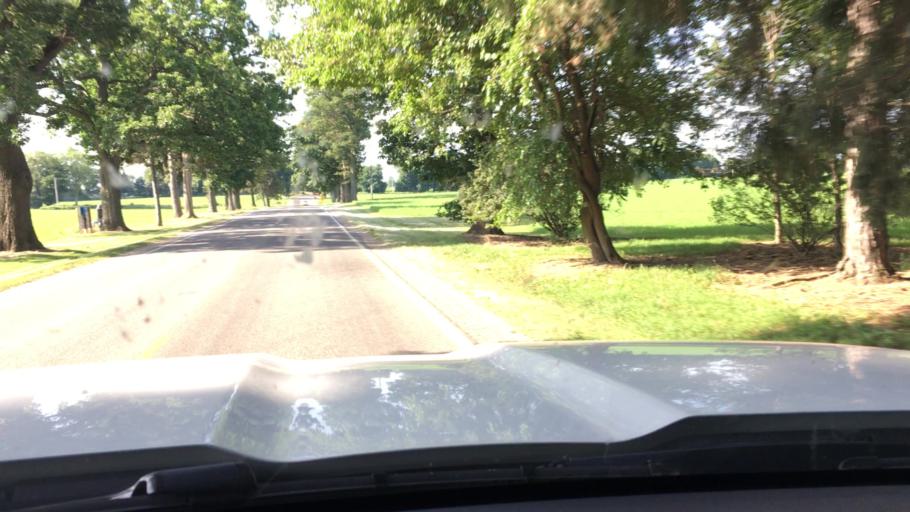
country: US
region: Michigan
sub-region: Kalamazoo County
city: South Gull Lake
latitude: 42.4255
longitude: -85.4546
